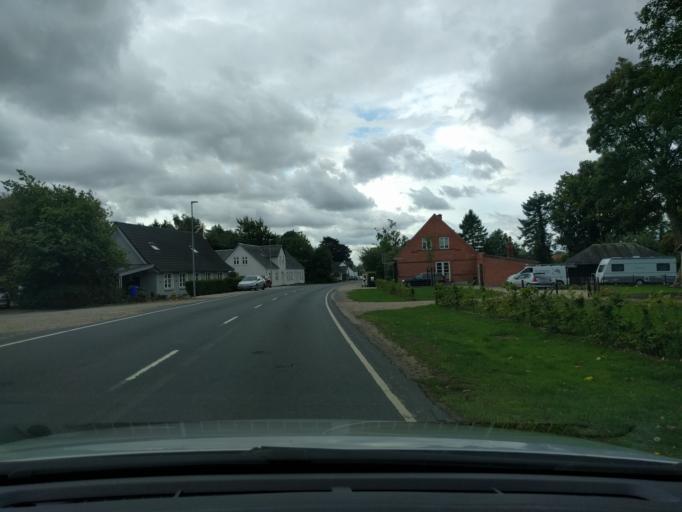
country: DK
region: South Denmark
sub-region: Nyborg Kommune
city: Ullerslev
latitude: 55.3833
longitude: 10.6675
